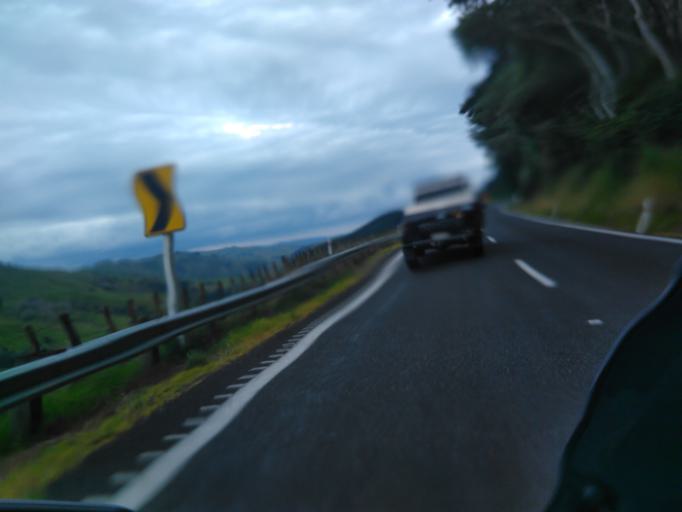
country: NZ
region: Gisborne
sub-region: Gisborne District
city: Gisborne
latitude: -38.4757
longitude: 177.6843
